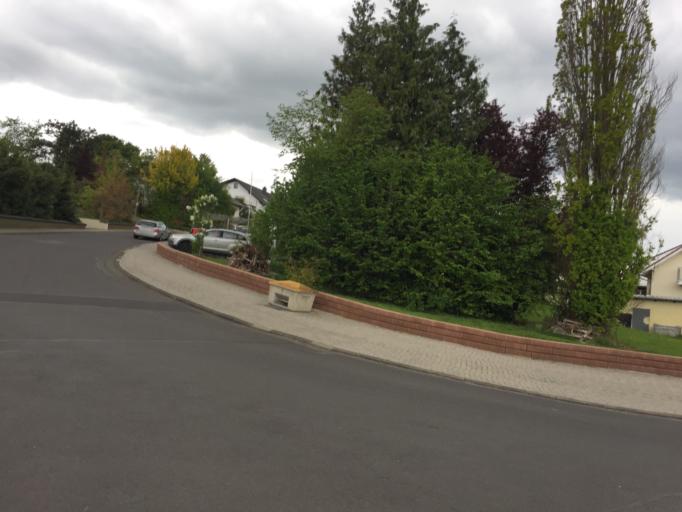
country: DE
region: Hesse
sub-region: Regierungsbezirk Giessen
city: Reiskirchen
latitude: 50.5750
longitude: 8.8541
